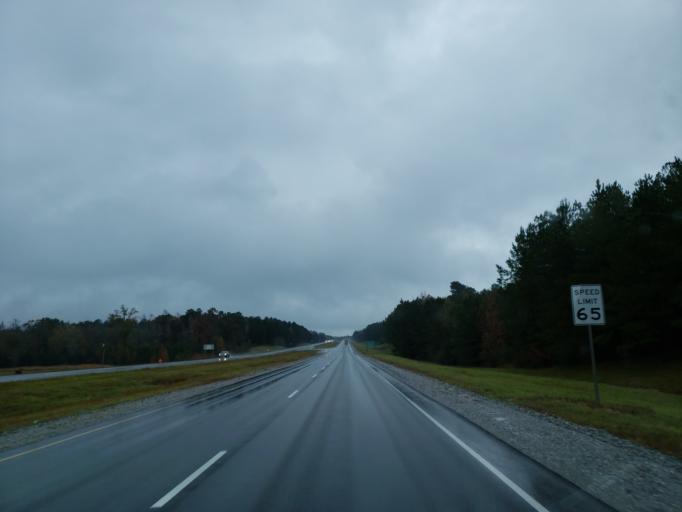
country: US
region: Mississippi
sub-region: Clarke County
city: Stonewall
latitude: 32.1832
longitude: -88.7090
